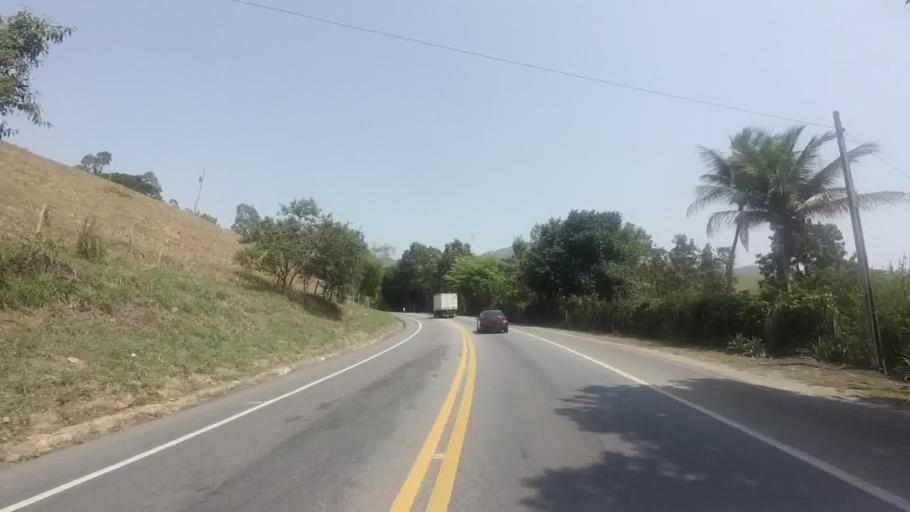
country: BR
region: Espirito Santo
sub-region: Iconha
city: Iconha
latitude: -20.7691
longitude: -40.7714
